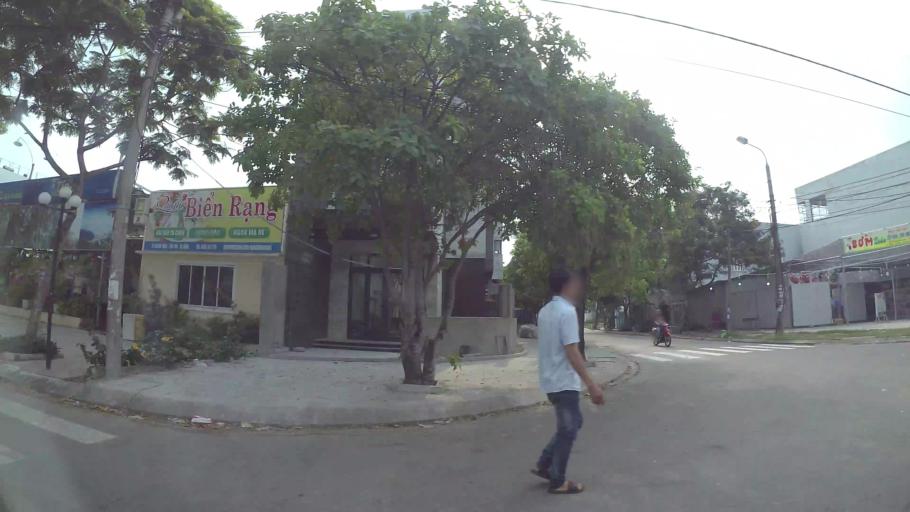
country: VN
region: Da Nang
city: Son Tra
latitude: 16.0869
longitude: 108.2465
